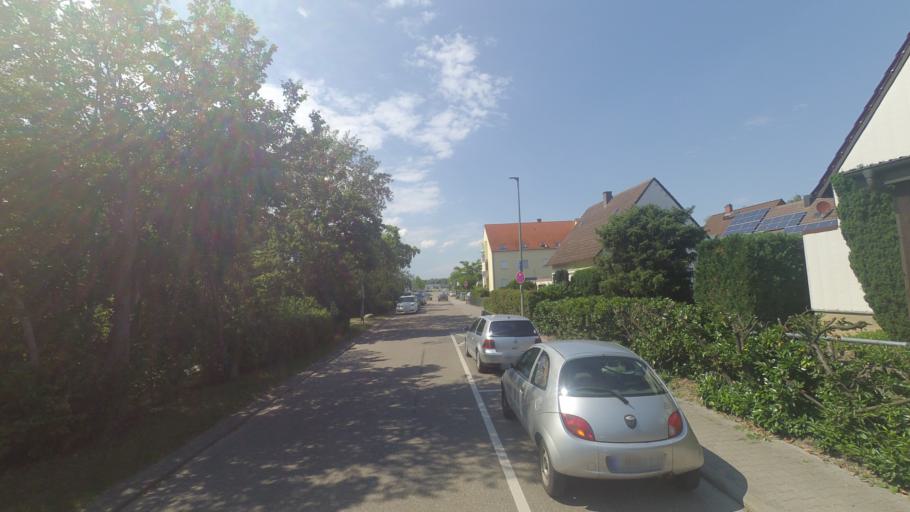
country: DE
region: Rheinland-Pfalz
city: Neuhofen
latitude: 49.4172
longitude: 8.4173
